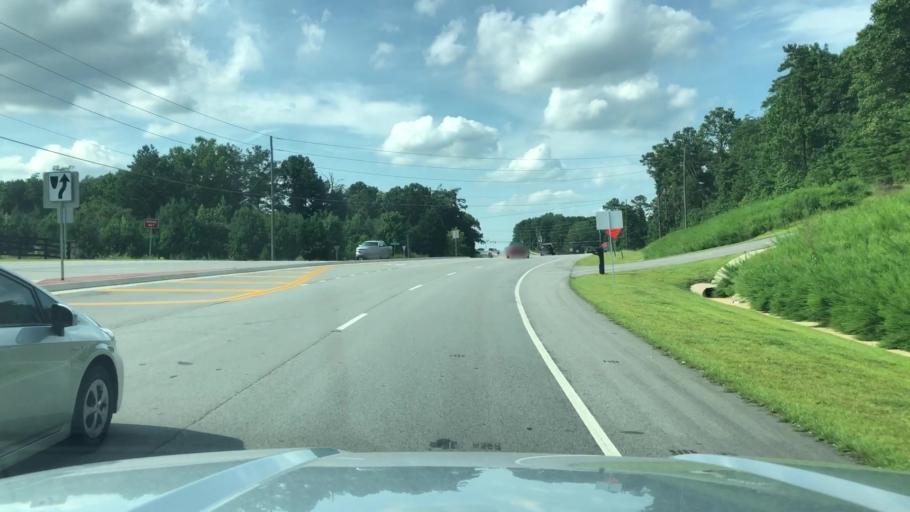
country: US
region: Georgia
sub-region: Paulding County
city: Hiram
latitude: 33.8639
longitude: -84.7809
